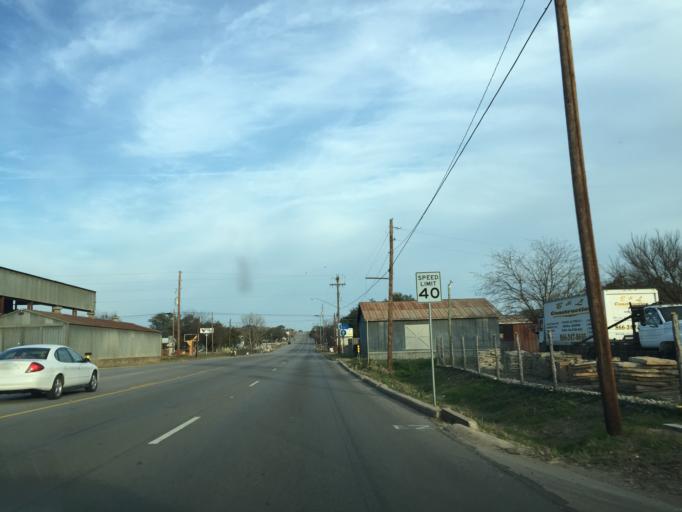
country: US
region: Texas
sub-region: Llano County
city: Llano
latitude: 30.7594
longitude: -98.6733
